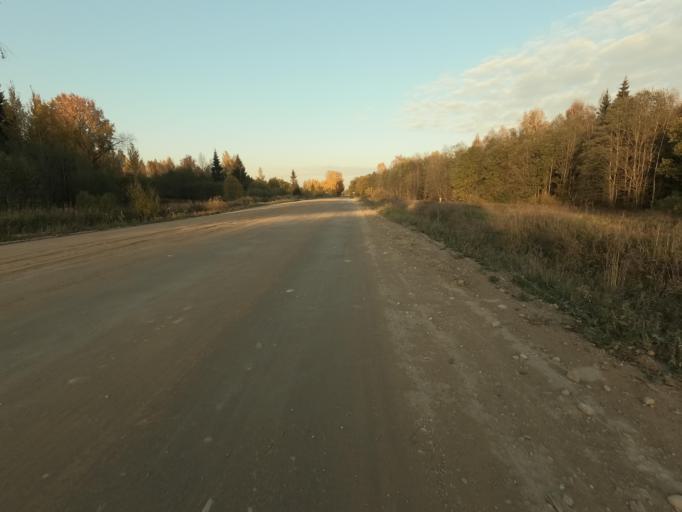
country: RU
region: Leningrad
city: Lyuban'
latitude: 59.0201
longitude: 31.0925
